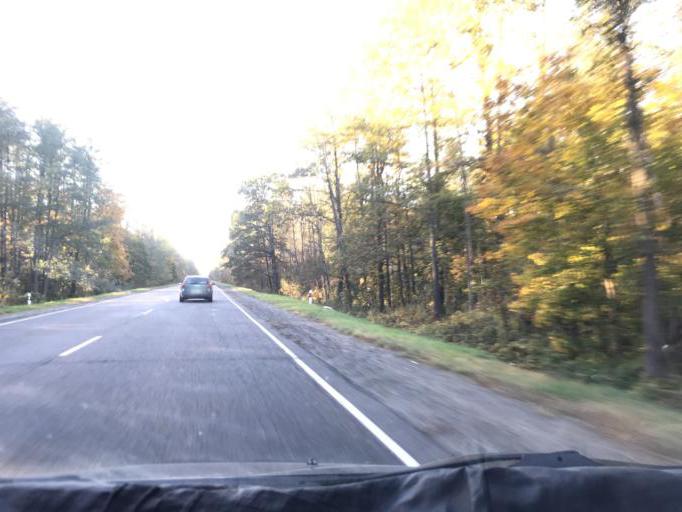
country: BY
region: Gomel
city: Pyetrykaw
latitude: 52.2647
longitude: 28.3071
